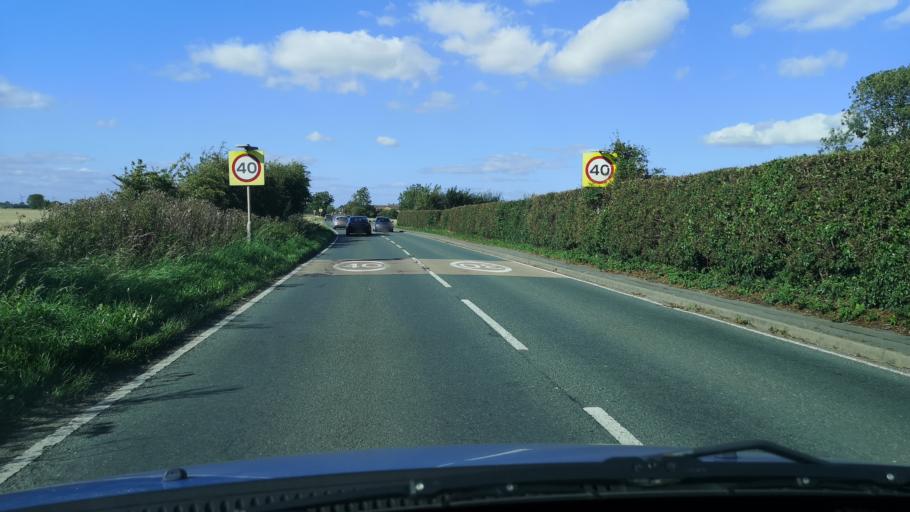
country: GB
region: England
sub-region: North Lincolnshire
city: Belton
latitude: 53.5578
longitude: -0.8168
